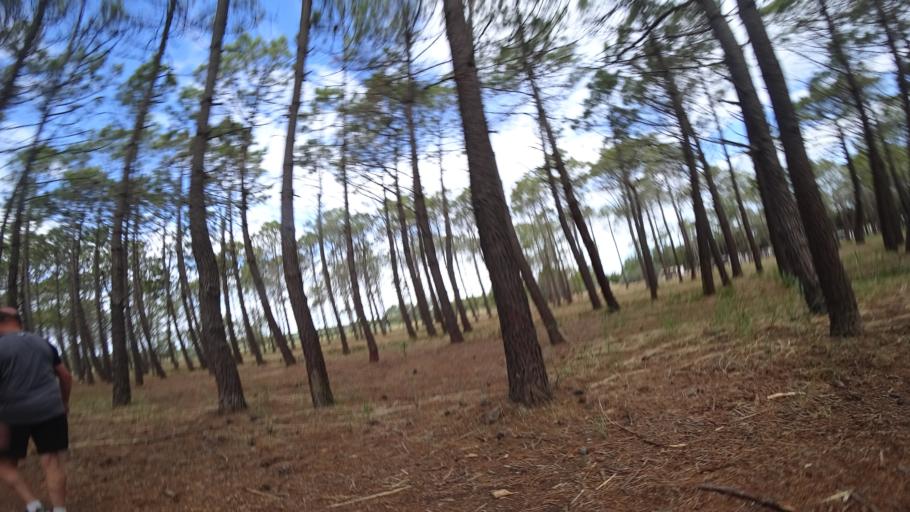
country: FR
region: Languedoc-Roussillon
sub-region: Departement des Pyrenees-Orientales
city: Le Barcares
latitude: 42.8193
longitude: 3.0340
